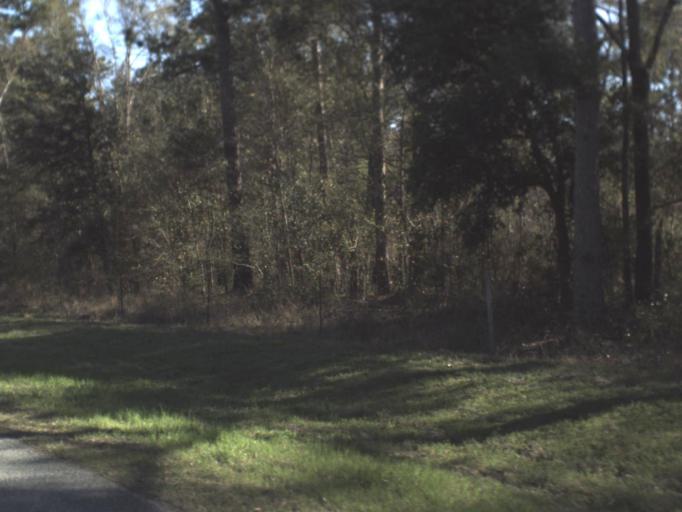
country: US
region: Georgia
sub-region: Brooks County
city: Quitman
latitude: 30.6508
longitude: -83.6425
